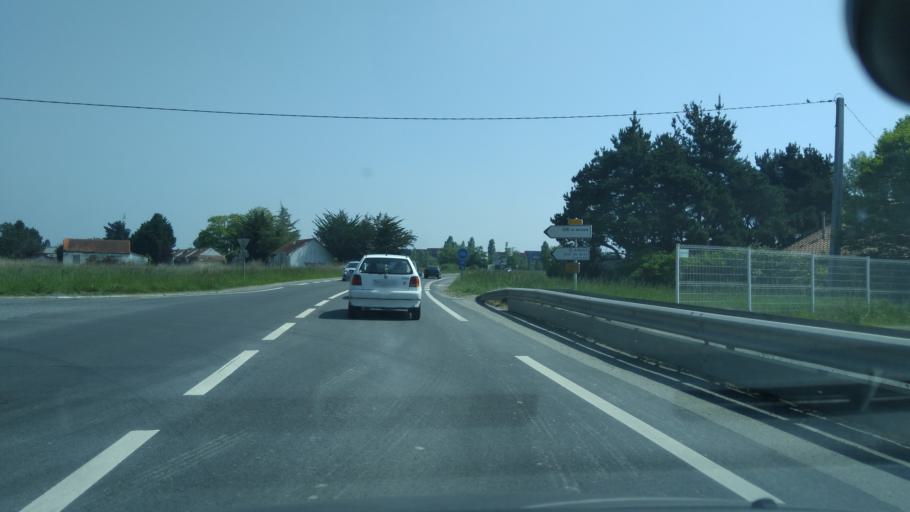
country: FR
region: Pays de la Loire
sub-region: Departement de la Loire-Atlantique
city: Montoir-de-Bretagne
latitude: 47.3171
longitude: -2.1666
